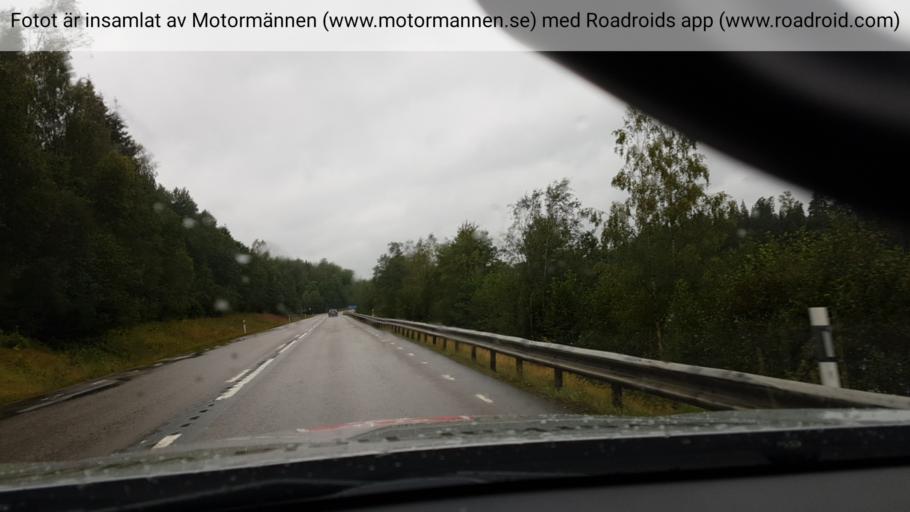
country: SE
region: Vaestra Goetaland
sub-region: Bengtsfors Kommun
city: Billingsfors
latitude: 58.9378
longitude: 12.0900
